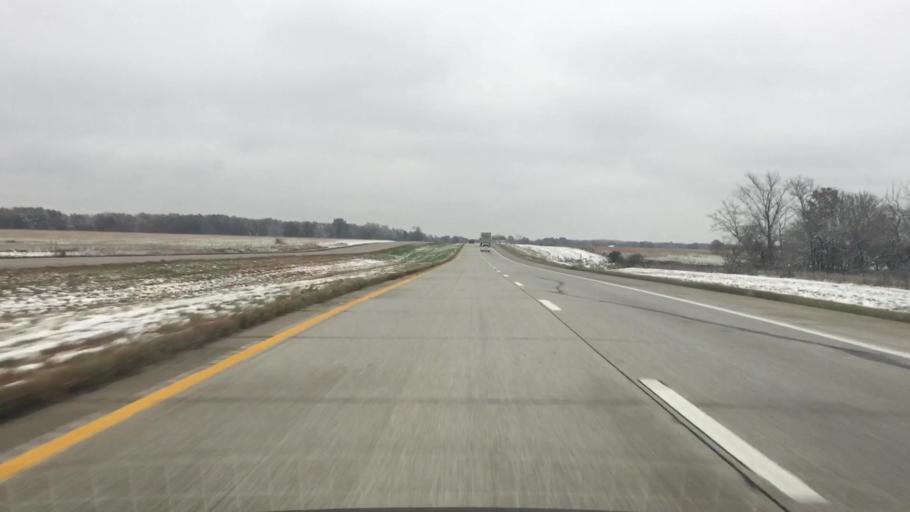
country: US
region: Missouri
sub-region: Henry County
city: Clinton
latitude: 38.4117
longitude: -93.8547
